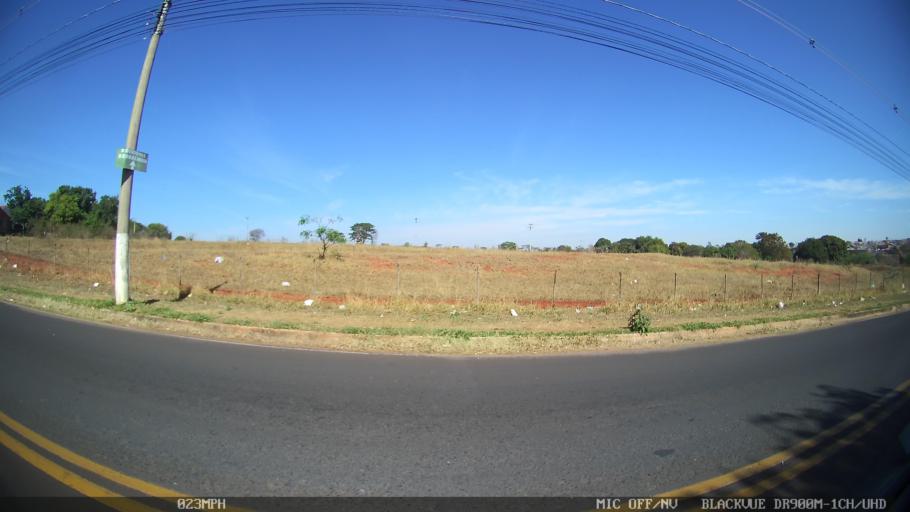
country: BR
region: Sao Paulo
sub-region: Sao Jose Do Rio Preto
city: Sao Jose do Rio Preto
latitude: -20.7663
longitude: -49.4231
